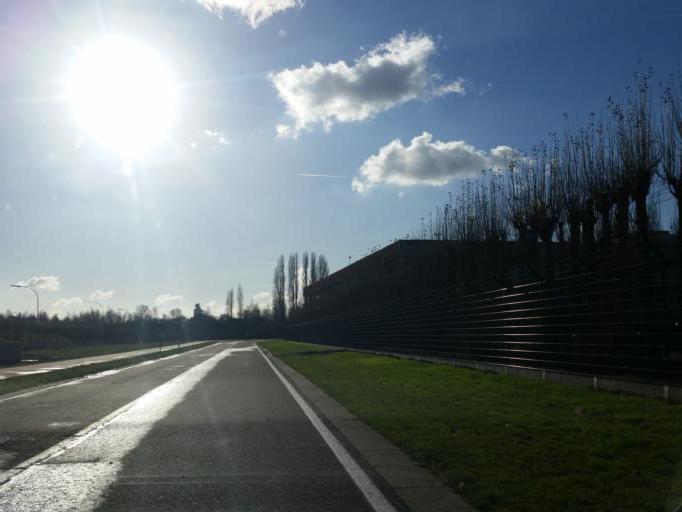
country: BE
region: Flanders
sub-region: Provincie Antwerpen
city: Zwijndrecht
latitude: 51.2489
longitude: 4.3136
